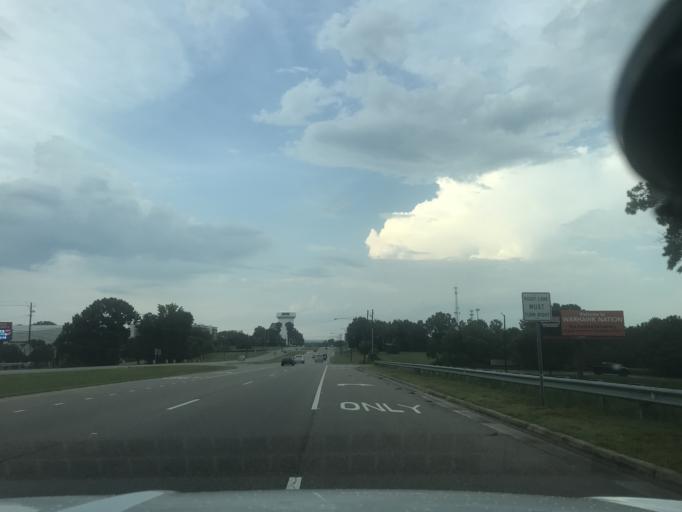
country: US
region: Alabama
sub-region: Montgomery County
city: Pike Road
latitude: 32.3642
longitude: -86.1711
